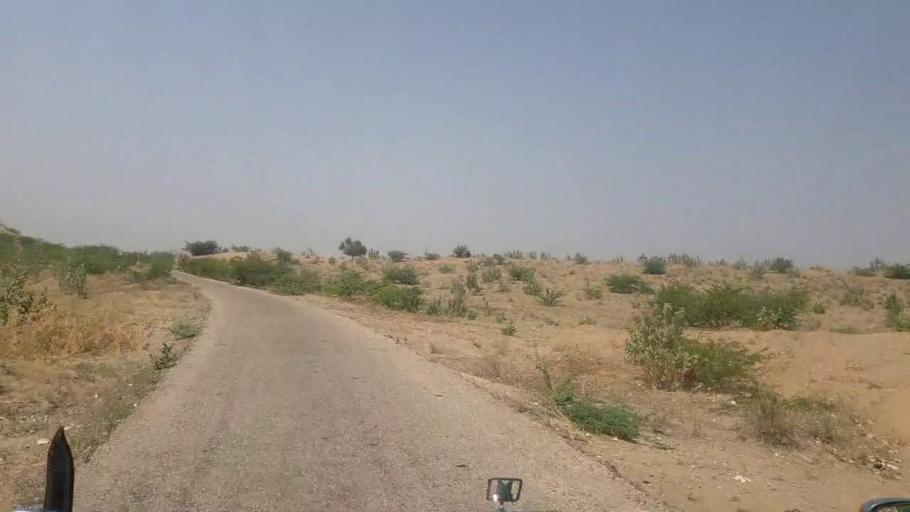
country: PK
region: Sindh
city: Islamkot
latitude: 25.1325
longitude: 70.2155
